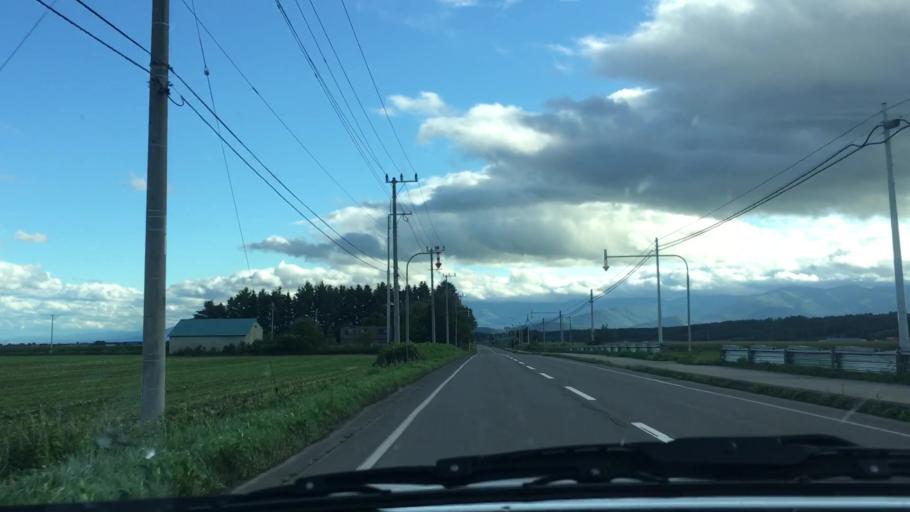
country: JP
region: Hokkaido
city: Otofuke
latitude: 43.1460
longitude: 142.8981
